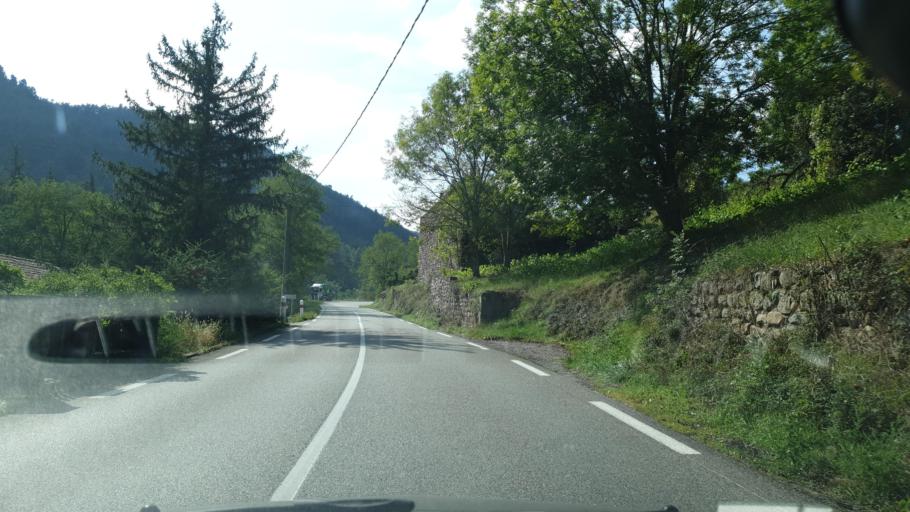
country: FR
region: Rhone-Alpes
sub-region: Departement de l'Ardeche
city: Saint-Sauveur-de-Montagut
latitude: 44.8133
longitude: 4.6397
